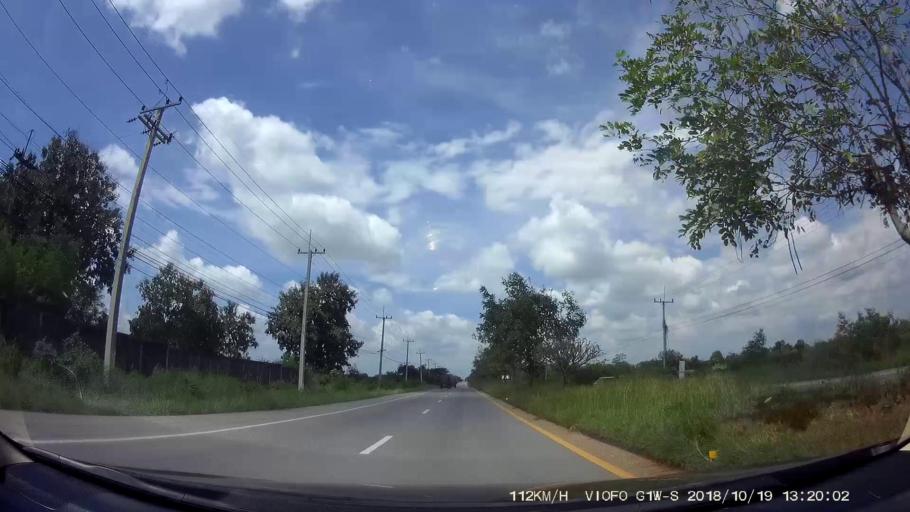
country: TH
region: Chaiyaphum
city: Chatturat
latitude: 15.4393
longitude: 101.8296
